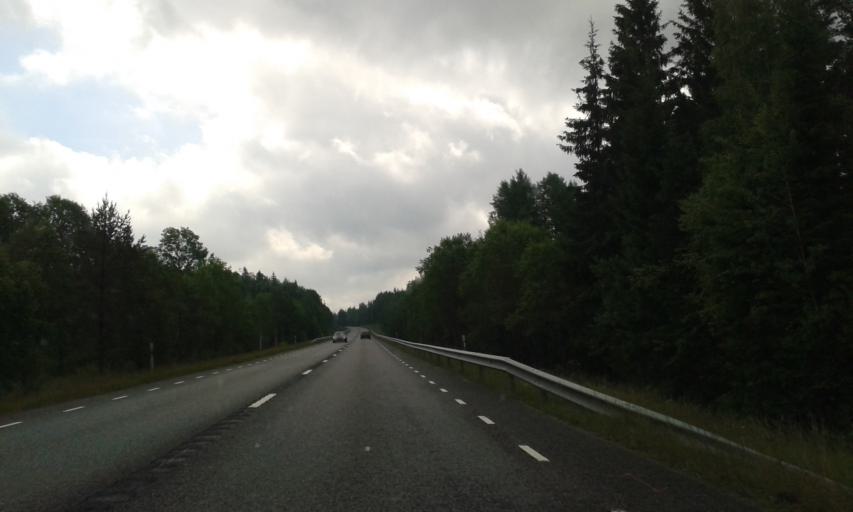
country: SE
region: Vaestra Goetaland
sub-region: Tranemo Kommun
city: Tranemo
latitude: 57.4523
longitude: 13.4106
